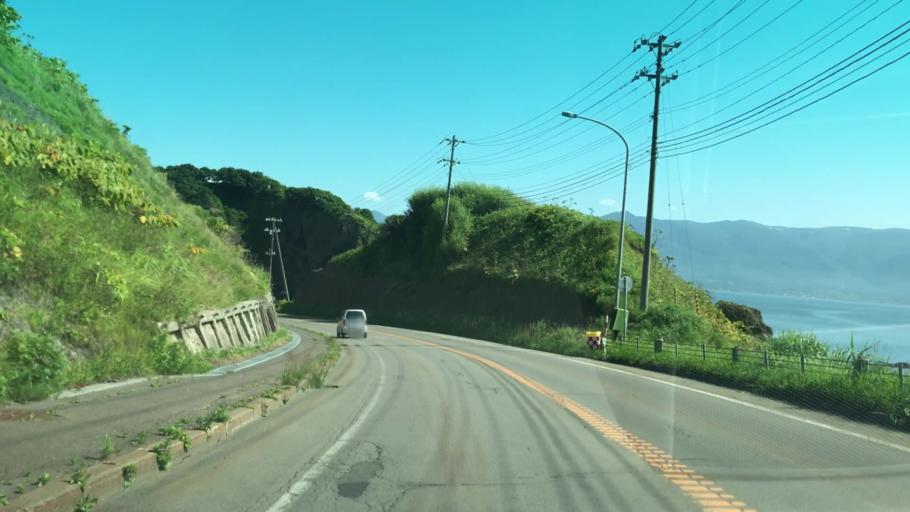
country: JP
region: Hokkaido
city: Iwanai
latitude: 43.0463
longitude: 140.5046
